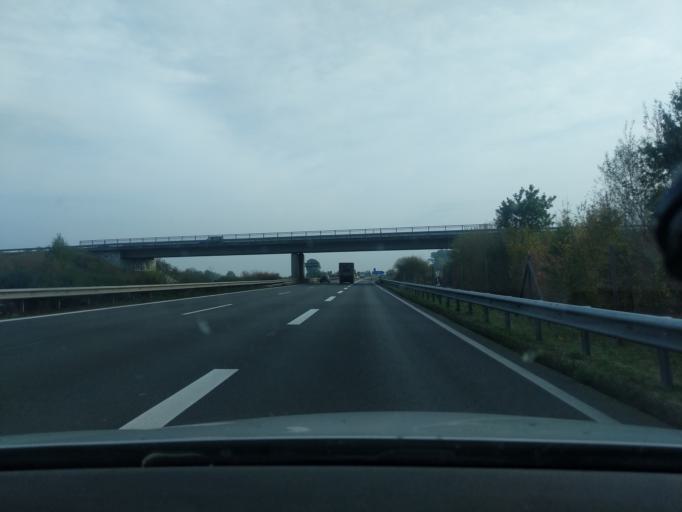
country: DE
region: Lower Saxony
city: Dollern
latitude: 53.5454
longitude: 9.5693
